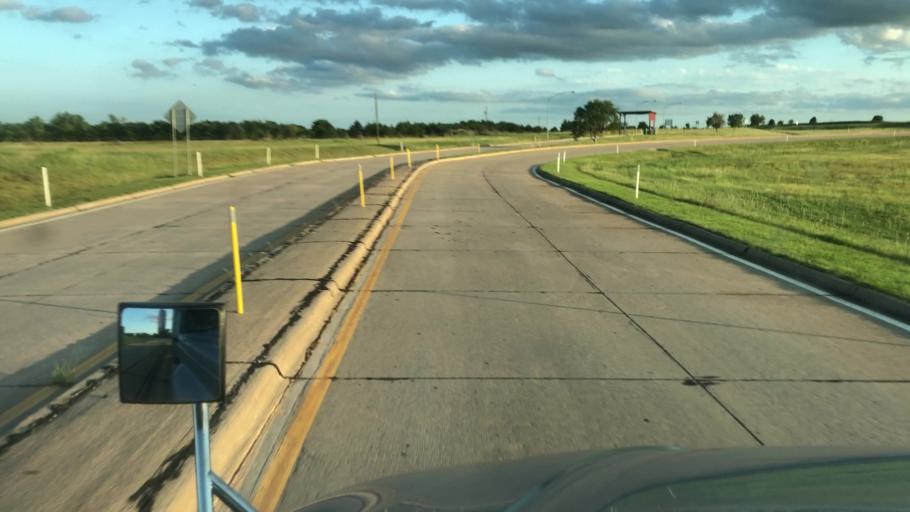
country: US
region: Oklahoma
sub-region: Pawnee County
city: Pawnee
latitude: 36.2973
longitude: -96.9842
